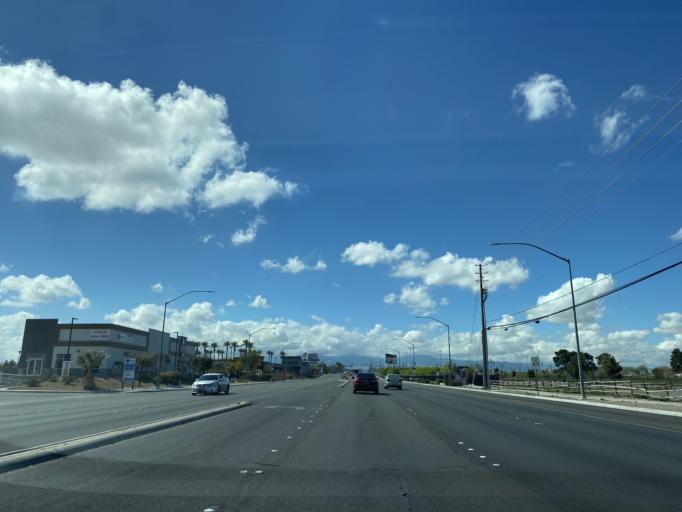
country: US
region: Nevada
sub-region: Clark County
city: North Las Vegas
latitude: 36.2395
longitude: -115.1478
